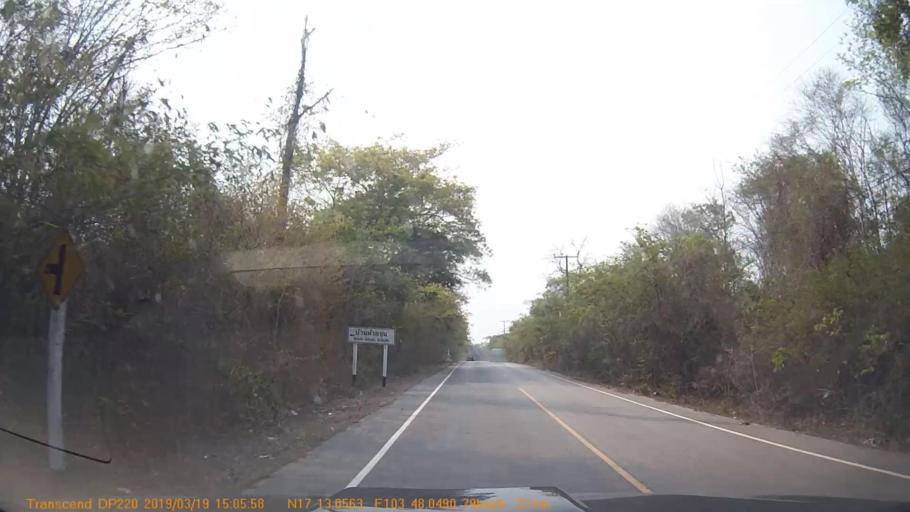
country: TH
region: Sakon Nakhon
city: Nikhom Nam Un
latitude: 17.2177
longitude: 103.8007
